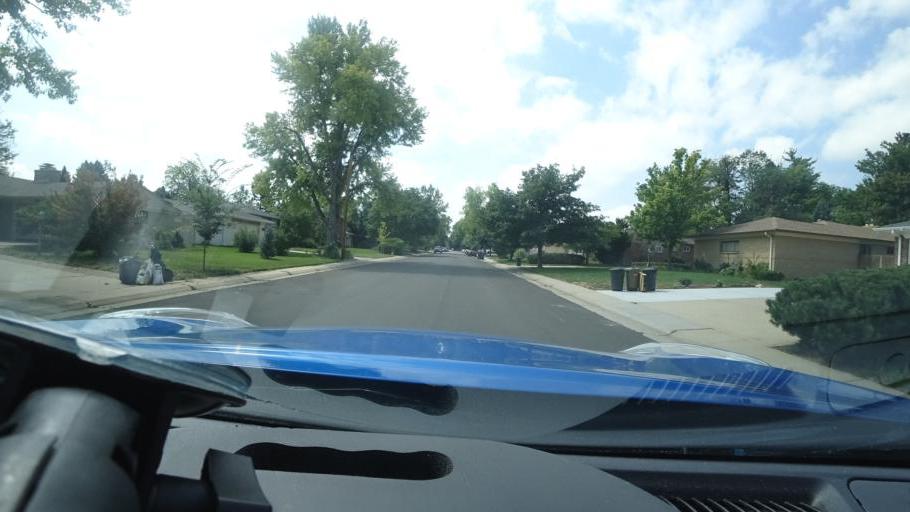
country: US
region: Colorado
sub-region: Adams County
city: Aurora
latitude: 39.7210
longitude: -104.8561
